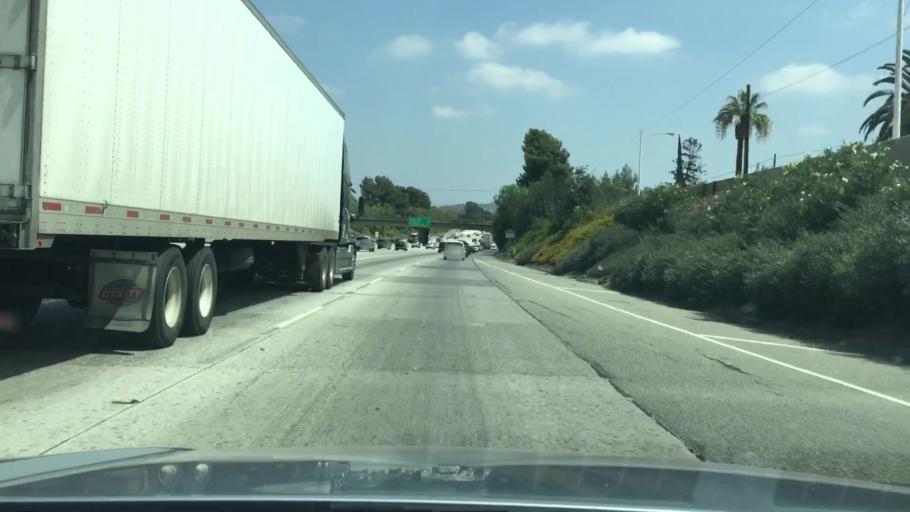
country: US
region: California
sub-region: Los Angeles County
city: Citrus
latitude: 34.1208
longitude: -117.9022
